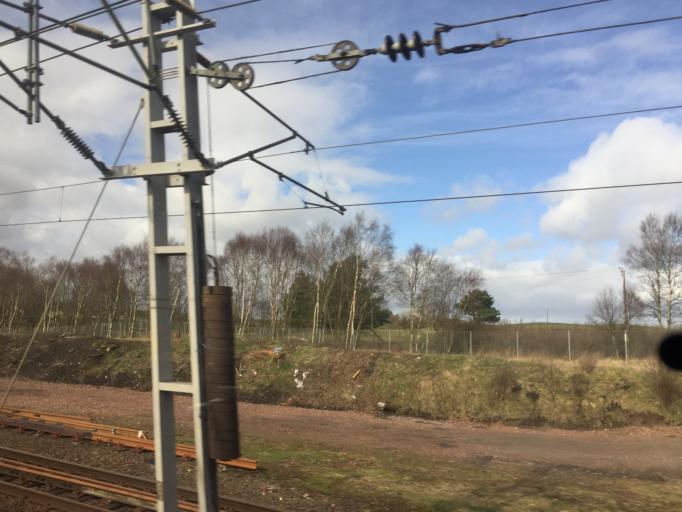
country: GB
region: Scotland
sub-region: South Lanarkshire
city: Carnwath
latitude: 55.6928
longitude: -3.6800
